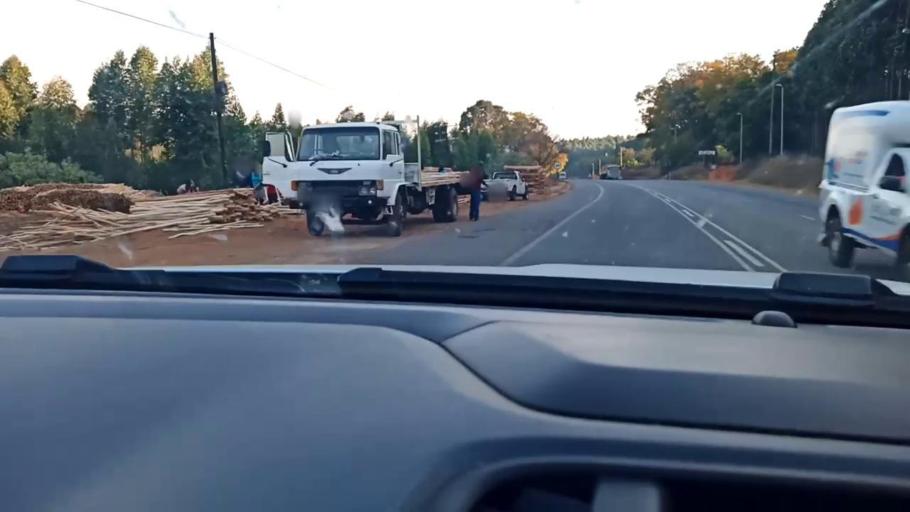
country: ZA
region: Limpopo
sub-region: Mopani District Municipality
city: Duiwelskloof
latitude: -23.7030
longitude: 30.1342
